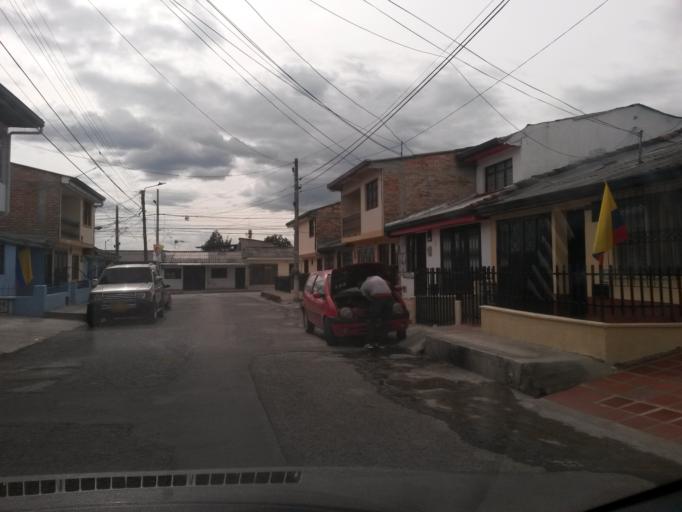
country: CO
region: Cauca
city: Popayan
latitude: 2.4509
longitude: -76.6239
